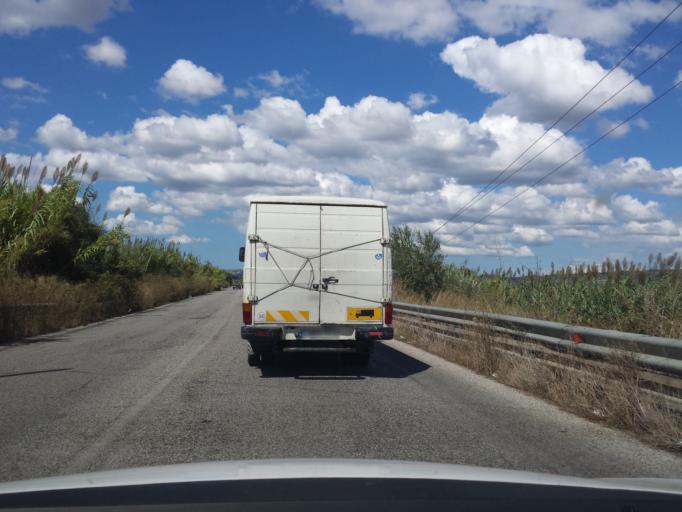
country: GR
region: West Greece
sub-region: Nomos Ileias
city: Epitalion
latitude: 37.6456
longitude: 21.4748
